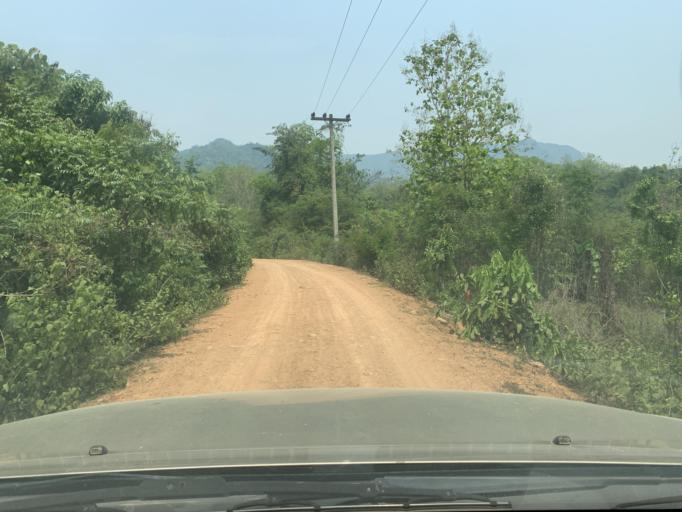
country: LA
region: Louangphabang
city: Louangphabang
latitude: 19.9664
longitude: 102.1270
